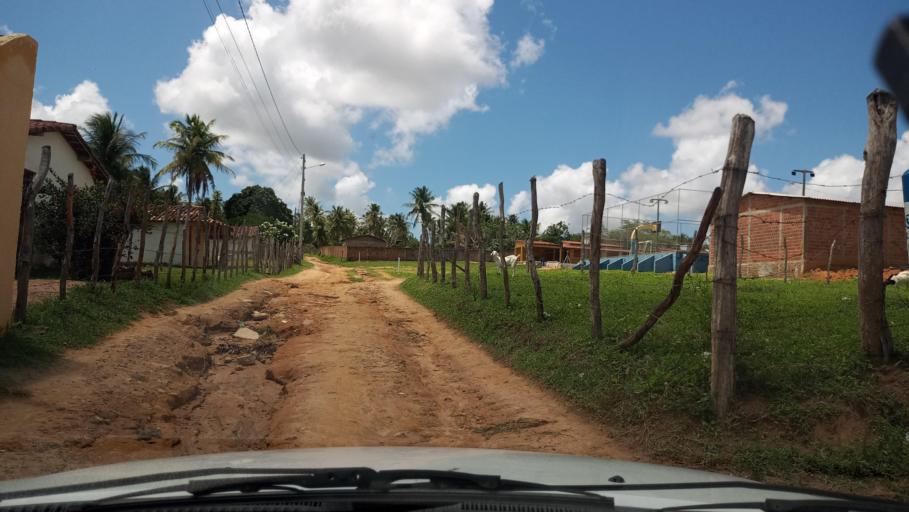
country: BR
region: Rio Grande do Norte
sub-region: Goianinha
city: Goianinha
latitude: -6.2972
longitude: -35.2227
